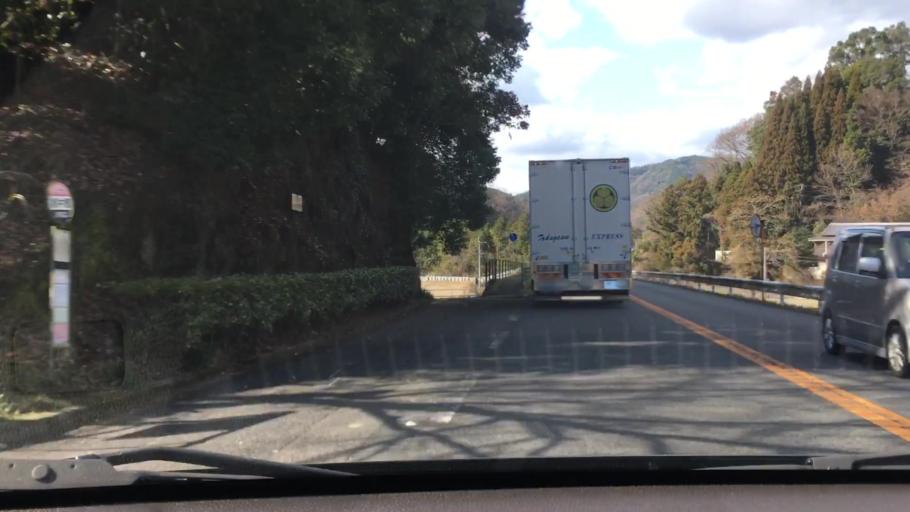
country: JP
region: Oita
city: Usuki
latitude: 32.9976
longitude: 131.7536
